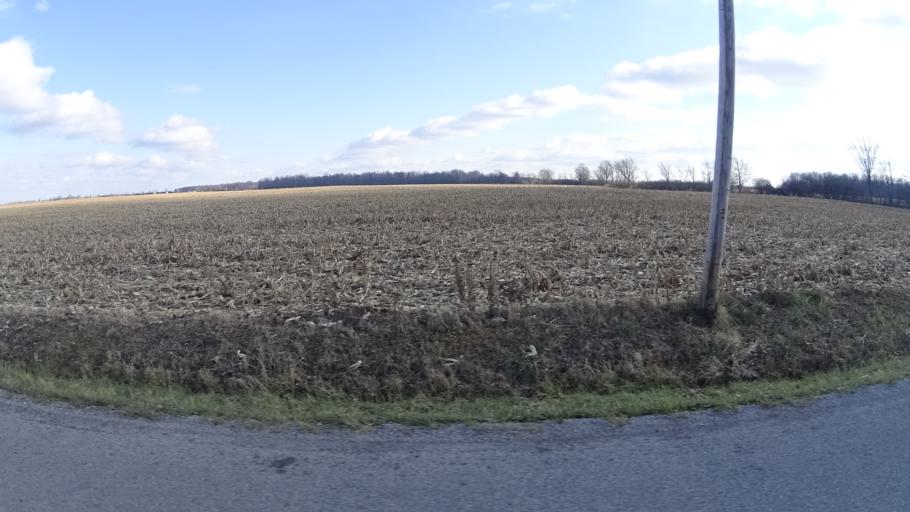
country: US
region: Ohio
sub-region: Lorain County
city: Camden
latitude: 41.2266
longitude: -82.2897
